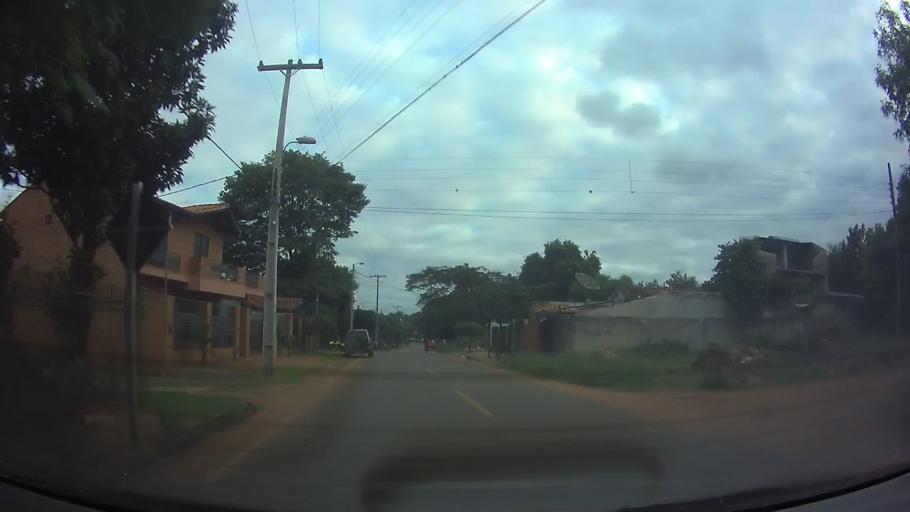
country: PY
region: Central
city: San Lorenzo
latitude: -25.2871
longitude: -57.4869
